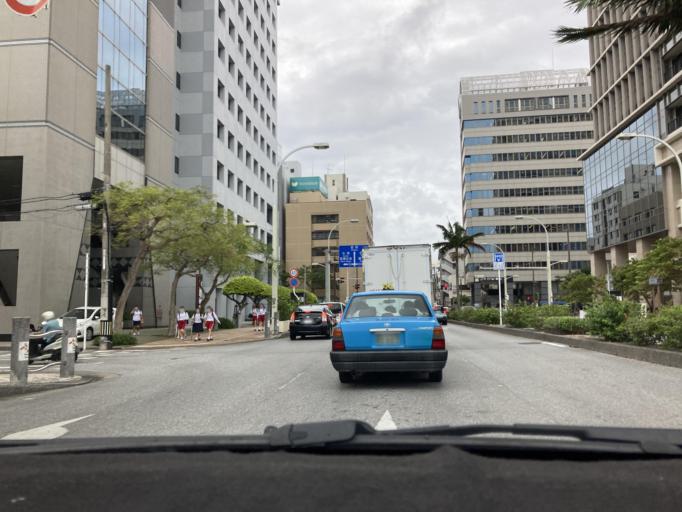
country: JP
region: Okinawa
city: Naha-shi
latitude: 26.2152
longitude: 127.6792
